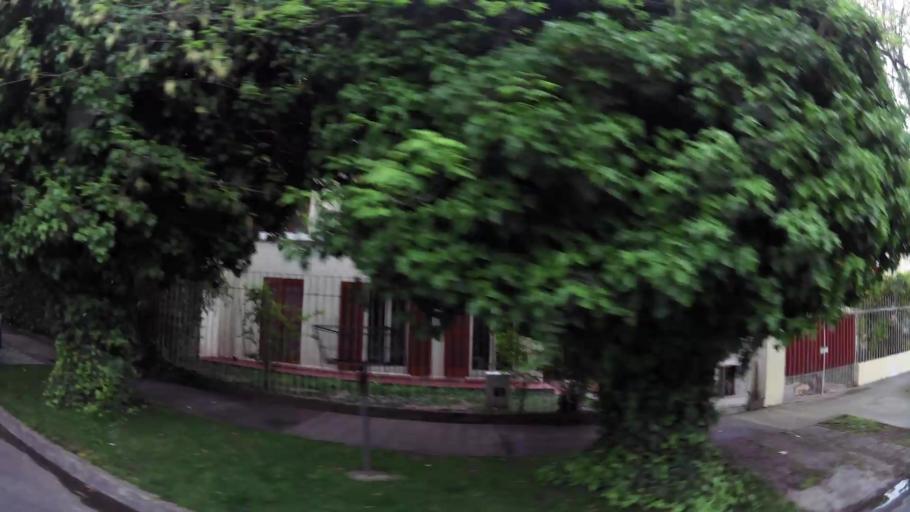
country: CL
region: Santiago Metropolitan
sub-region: Provincia de Santiago
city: Villa Presidente Frei, Nunoa, Santiago, Chile
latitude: -33.4597
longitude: -70.5911
